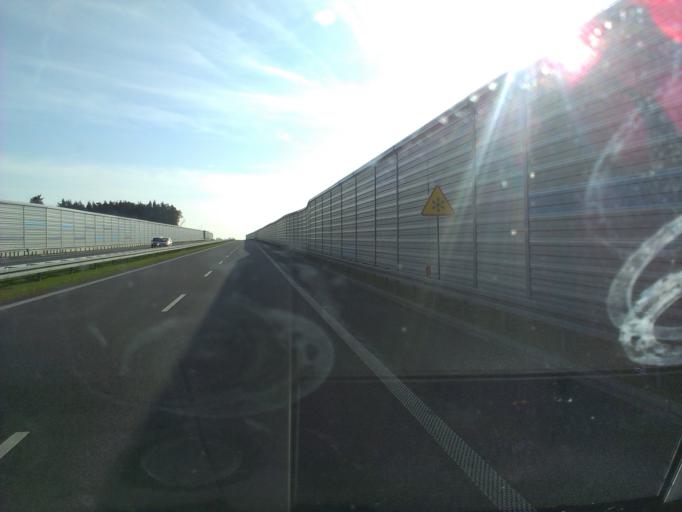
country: PL
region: West Pomeranian Voivodeship
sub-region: Powiat pyrzycki
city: Lipiany
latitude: 52.9663
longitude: 14.9172
